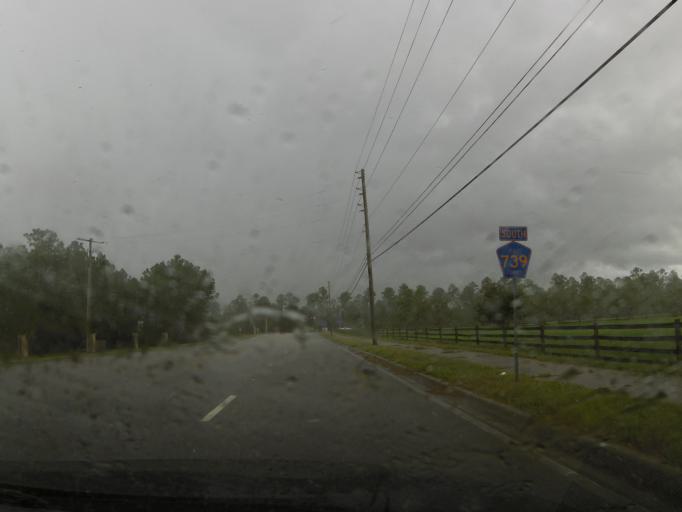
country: US
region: Florida
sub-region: Clay County
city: Asbury Lake
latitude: 30.0320
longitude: -81.8099
